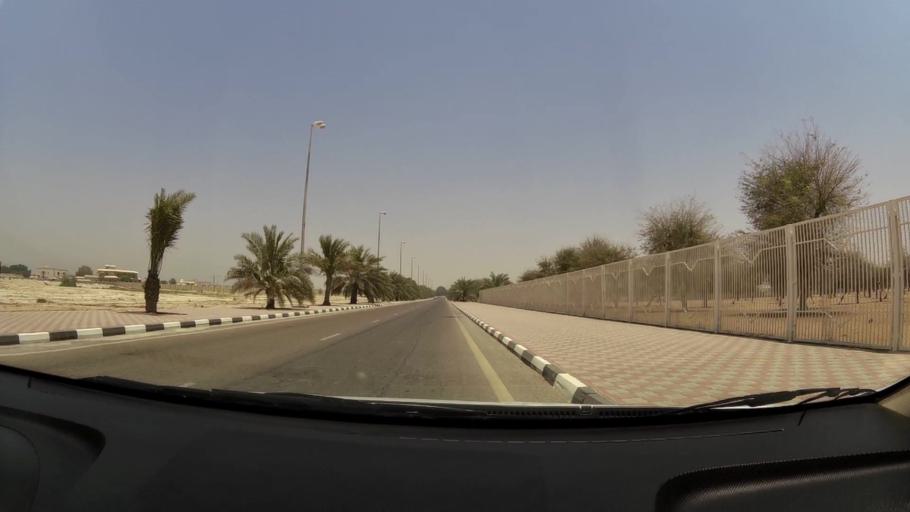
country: AE
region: Umm al Qaywayn
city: Umm al Qaywayn
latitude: 25.5310
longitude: 55.5317
